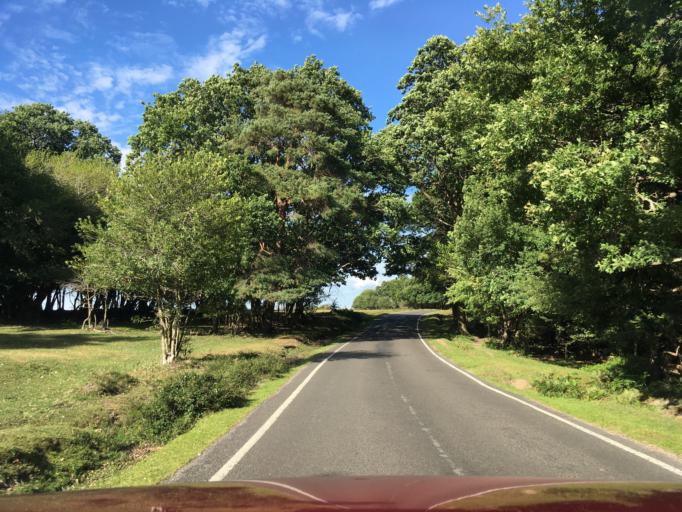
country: GB
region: England
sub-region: Hampshire
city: Cadnam
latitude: 50.9340
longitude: -1.6506
